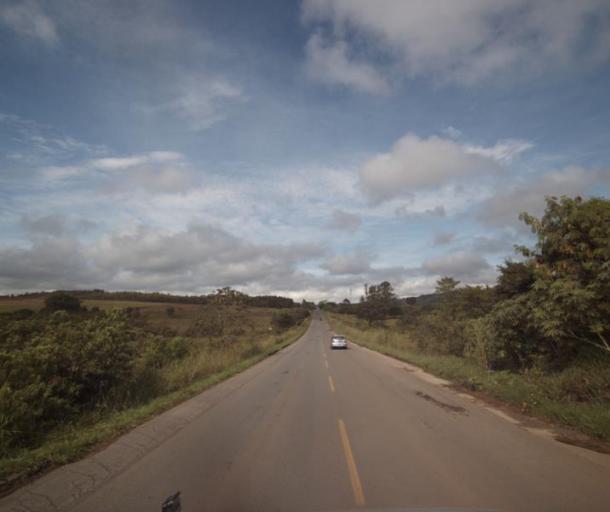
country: BR
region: Goias
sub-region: Pirenopolis
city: Pirenopolis
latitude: -15.7944
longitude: -48.7748
